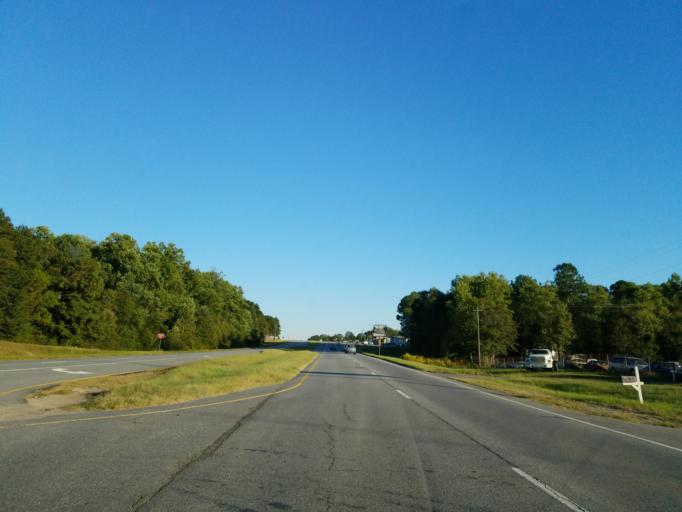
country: US
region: Georgia
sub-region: Worth County
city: Sylvester
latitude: 31.5216
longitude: -83.7893
